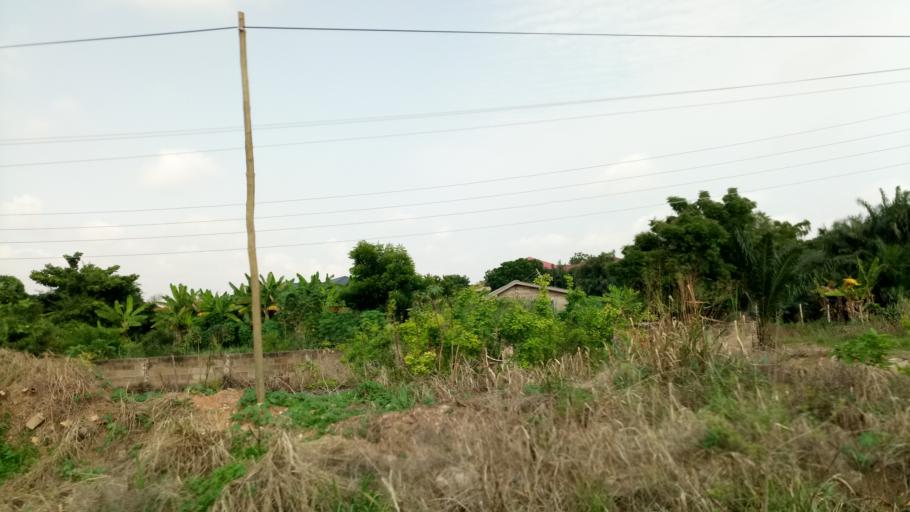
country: GH
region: Greater Accra
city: Medina Estates
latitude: 5.6775
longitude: -0.1918
